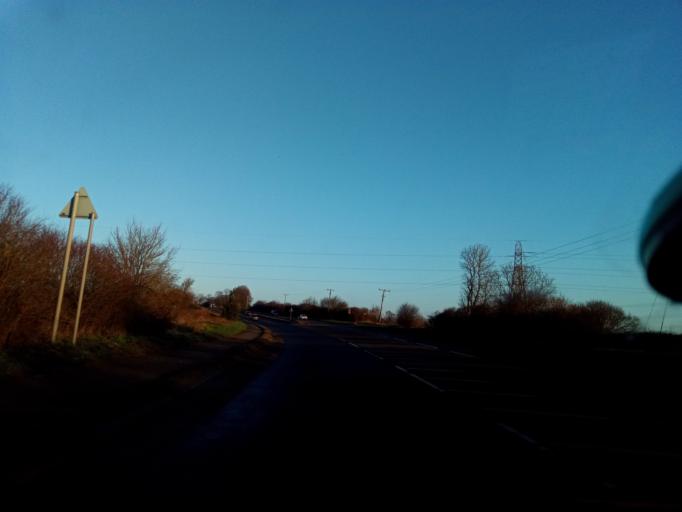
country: GB
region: England
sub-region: Leicestershire
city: Hathern
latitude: 52.8029
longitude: -1.2619
